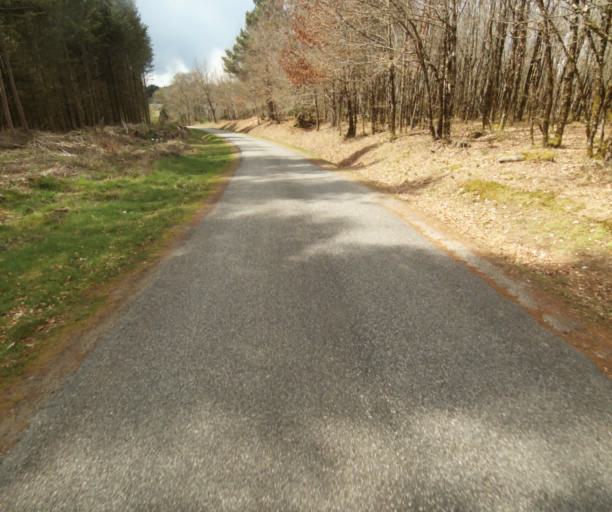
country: FR
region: Limousin
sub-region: Departement de la Correze
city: Correze
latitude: 45.2740
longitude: 1.9724
